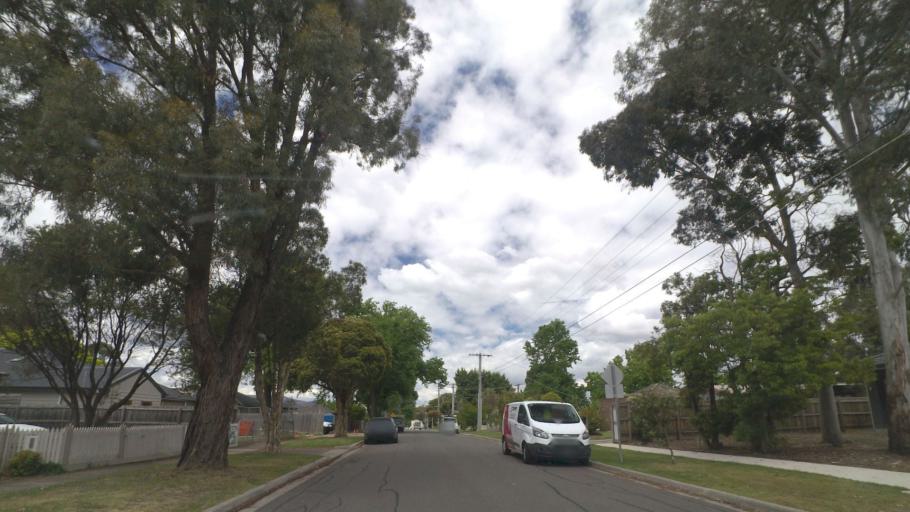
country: AU
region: Victoria
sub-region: Yarra Ranges
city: Kilsyth
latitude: -37.7986
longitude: 145.3045
